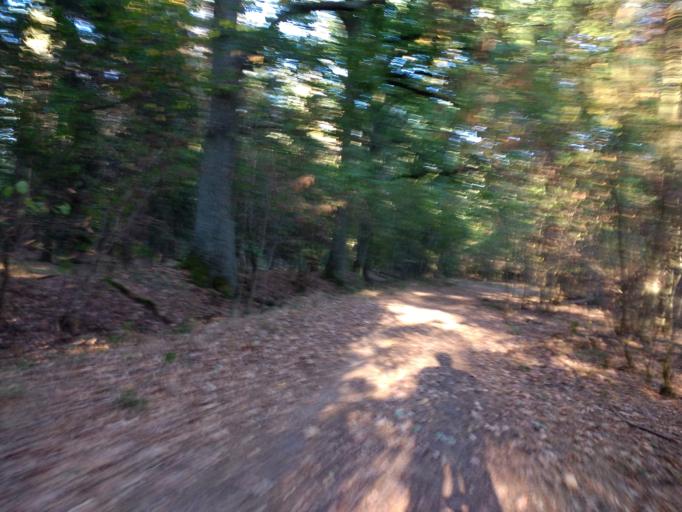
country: DE
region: Lower Saxony
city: Gifhorn
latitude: 52.4598
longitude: 10.5508
